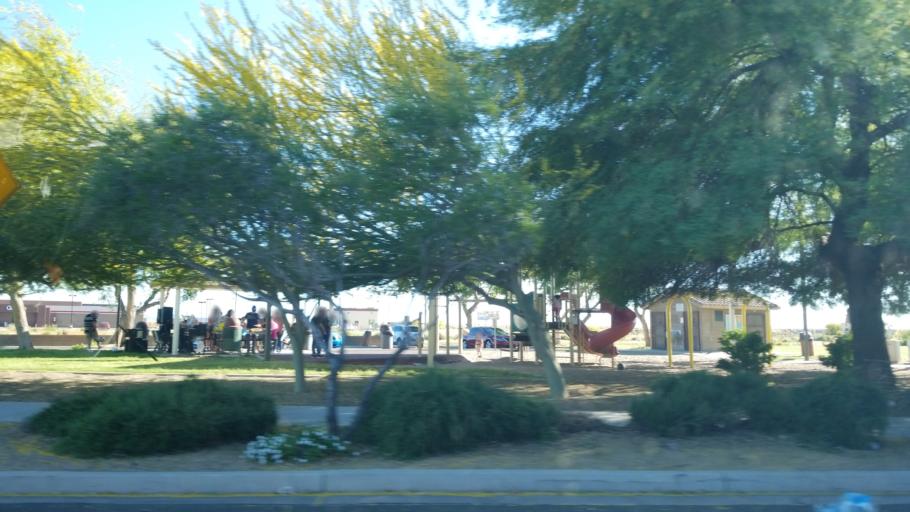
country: US
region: Arizona
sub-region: Maricopa County
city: Youngtown
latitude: 33.5677
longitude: -112.3099
